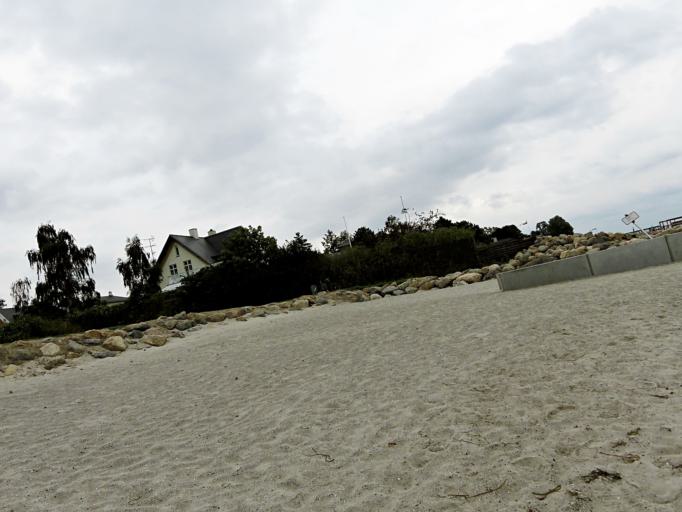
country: DK
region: Capital Region
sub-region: Rudersdal Kommune
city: Trorod
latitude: 55.8520
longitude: 12.5692
